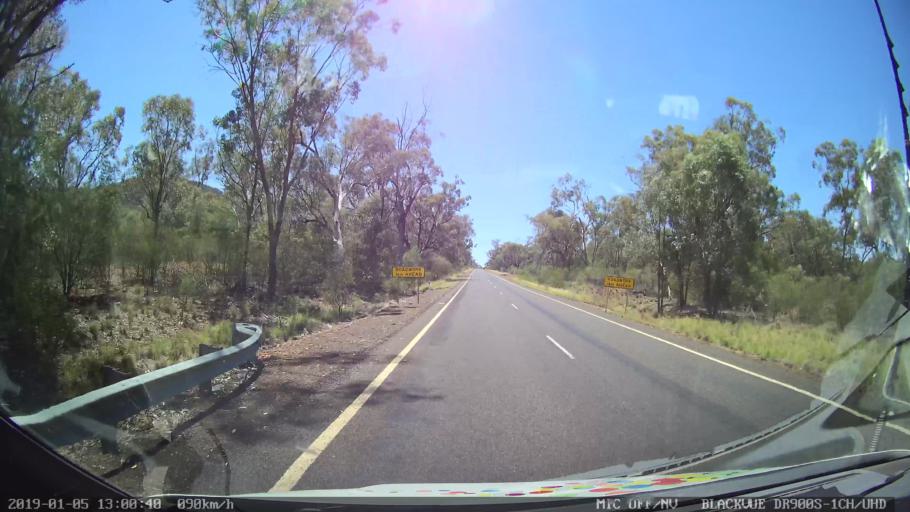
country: AU
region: New South Wales
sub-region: Narrabri
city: Boggabri
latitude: -31.1148
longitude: 149.7858
